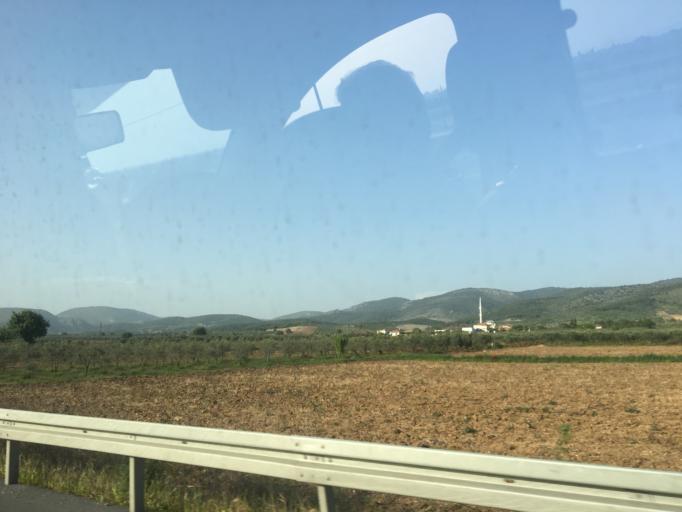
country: TR
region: Manisa
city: Golmarmara
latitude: 38.7905
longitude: 27.9012
